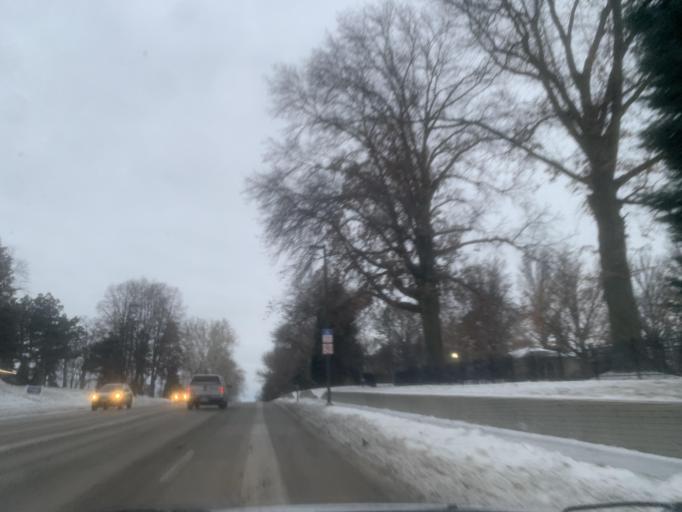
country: US
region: Nebraska
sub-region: Douglas County
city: Ralston
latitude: 41.2597
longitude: -96.0526
